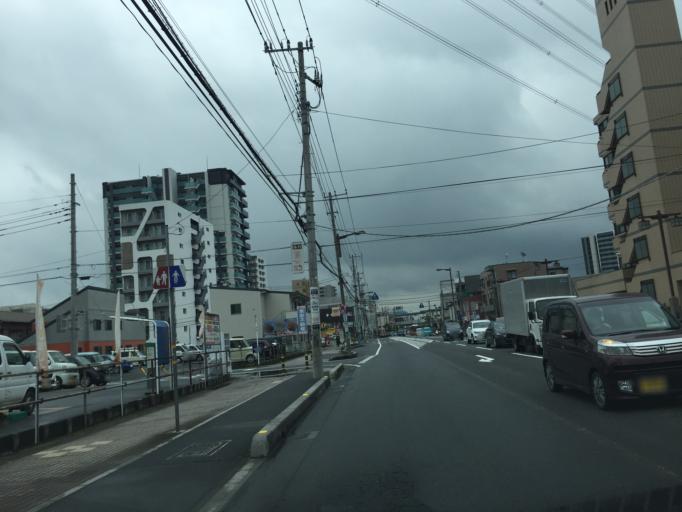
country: JP
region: Saitama
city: Koshigaya
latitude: 35.8779
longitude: 139.7427
